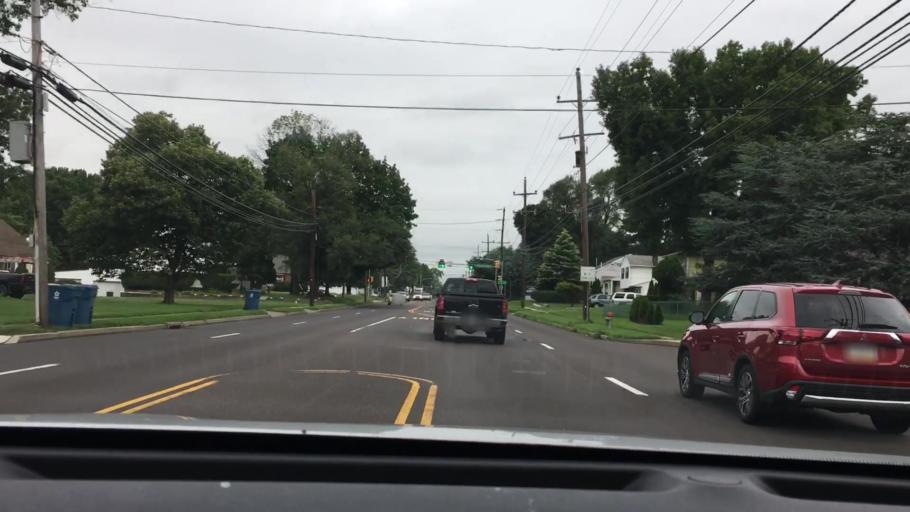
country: US
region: Pennsylvania
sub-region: Montgomery County
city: Horsham
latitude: 40.1971
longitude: -75.1149
